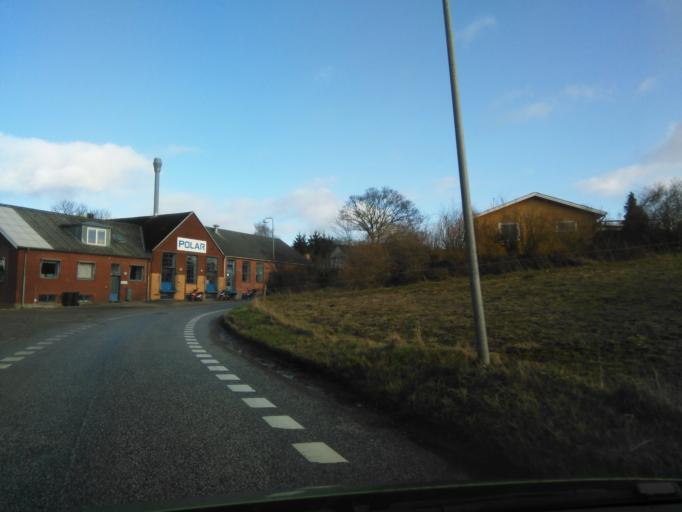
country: DK
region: Central Jutland
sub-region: Skanderborg Kommune
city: Skanderborg
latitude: 55.9946
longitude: 9.9297
